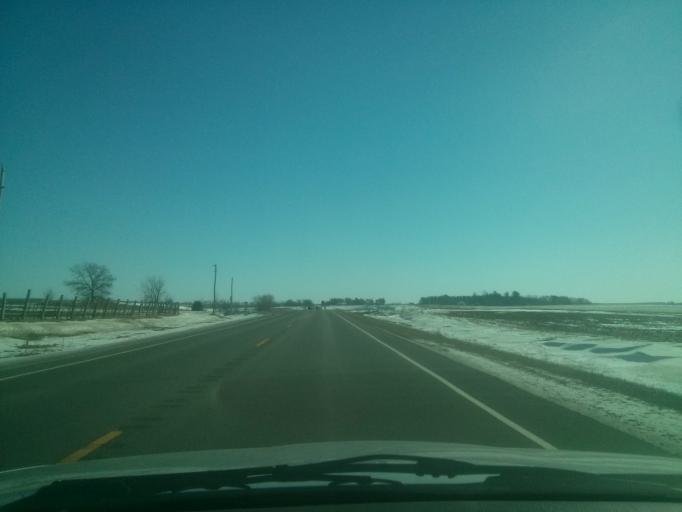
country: US
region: Wisconsin
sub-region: Polk County
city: Clear Lake
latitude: 45.1363
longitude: -92.3645
